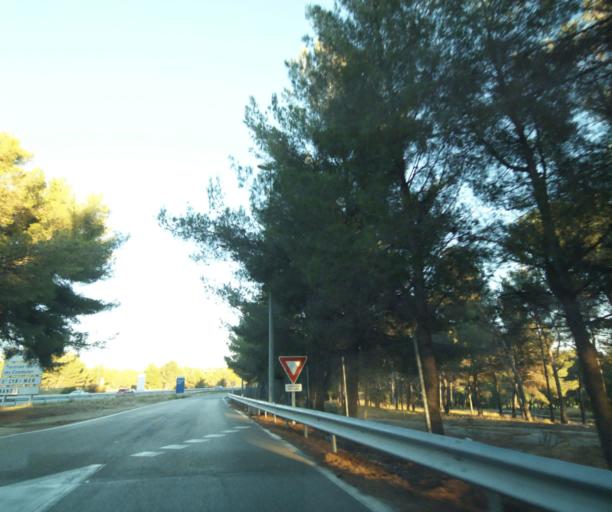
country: FR
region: Provence-Alpes-Cote d'Azur
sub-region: Departement du Var
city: Saint-Cyr-sur-Mer
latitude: 43.1927
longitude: 5.6707
